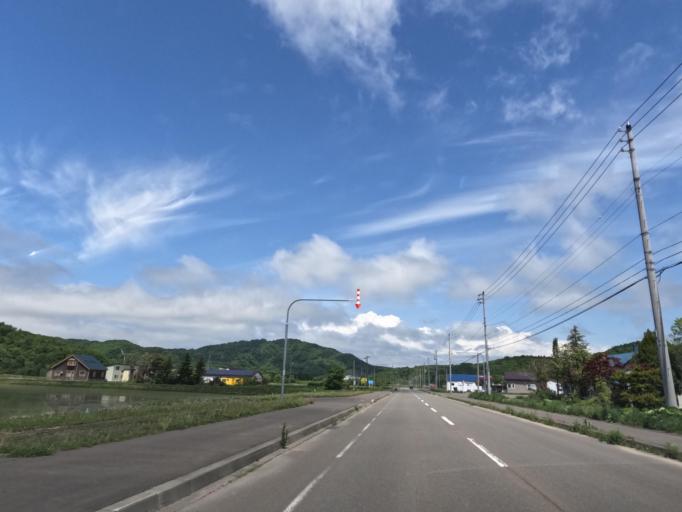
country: JP
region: Hokkaido
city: Tobetsu
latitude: 43.3019
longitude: 141.5499
